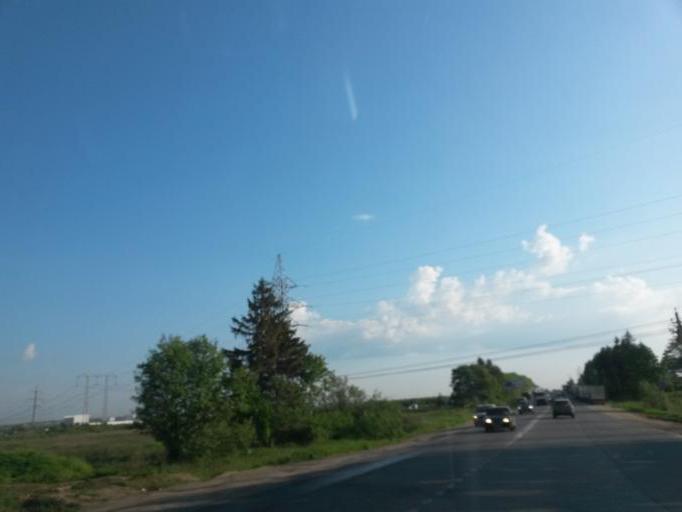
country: RU
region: Moskovskaya
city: Yam
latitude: 55.4731
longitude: 37.7121
